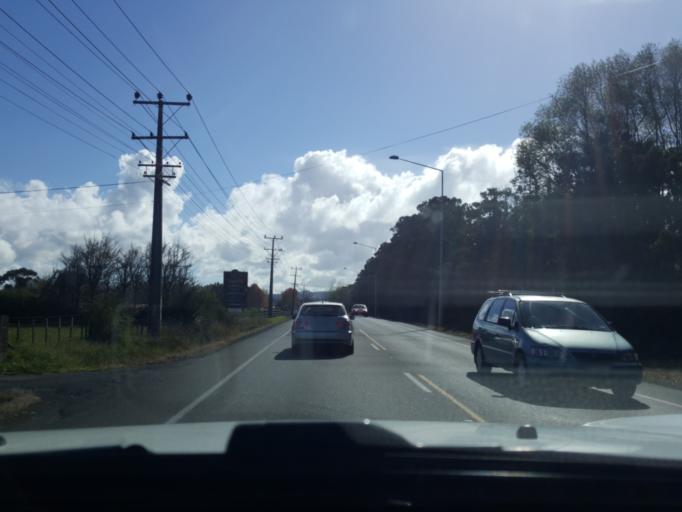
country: NZ
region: Auckland
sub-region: Auckland
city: Muriwai Beach
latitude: -36.7853
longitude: 174.5720
